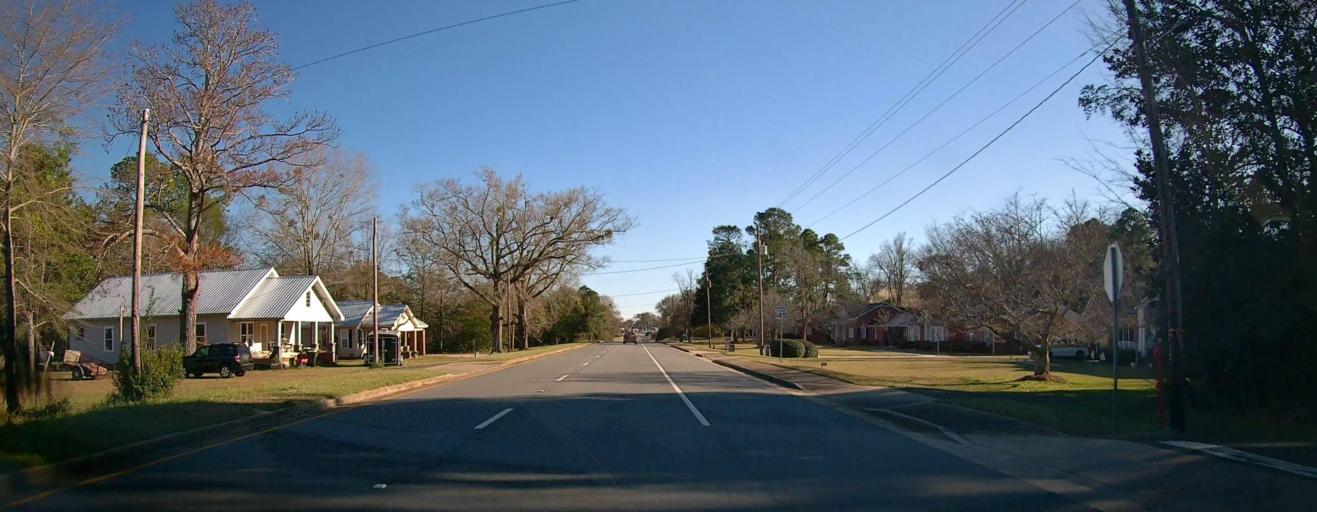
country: US
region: Georgia
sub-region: Taylor County
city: Butler
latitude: 32.5643
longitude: -84.2395
